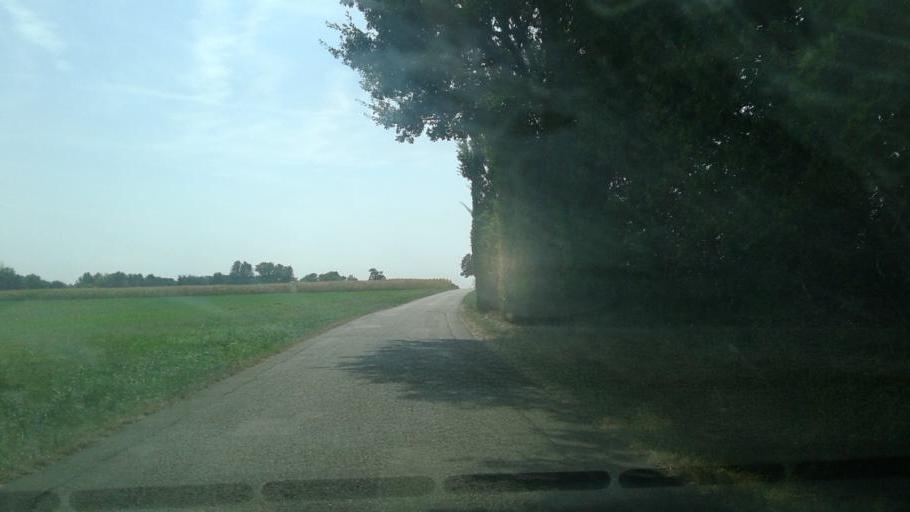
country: FR
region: Rhone-Alpes
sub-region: Departement de l'Ain
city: Saint-Maurice-de-Beynost
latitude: 45.8483
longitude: 4.9732
